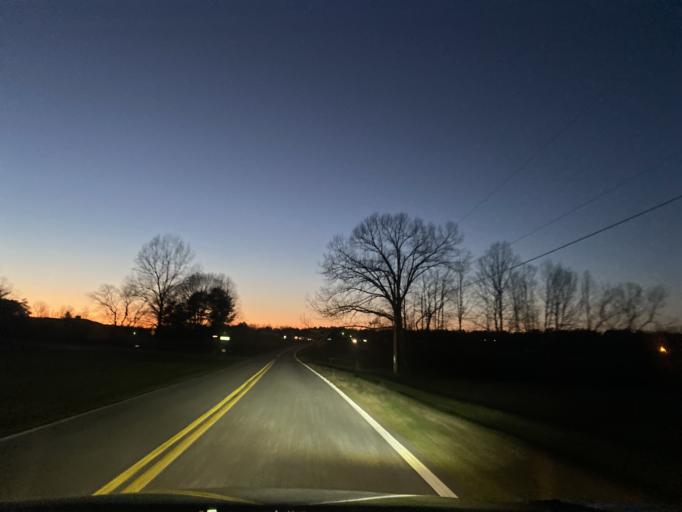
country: US
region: South Carolina
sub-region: Cherokee County
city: Gaffney
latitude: 35.1350
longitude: -81.7142
